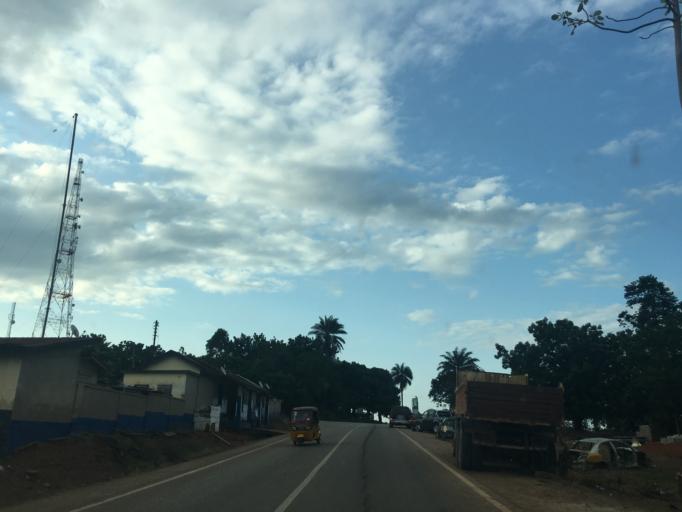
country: GH
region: Western
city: Bibiani
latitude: 6.4578
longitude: -2.3173
